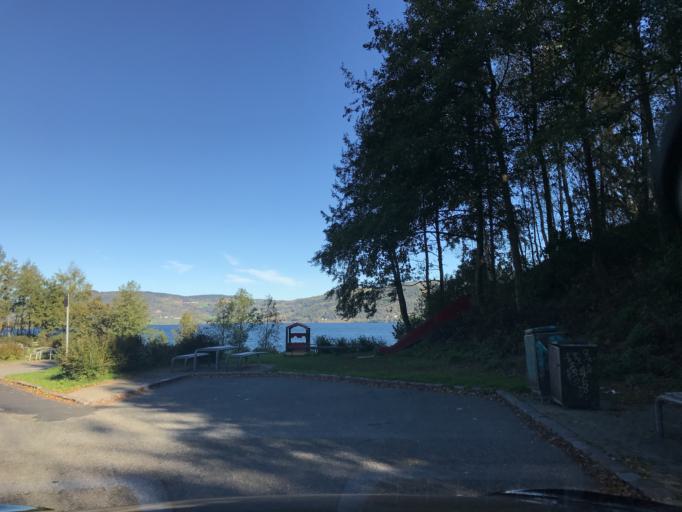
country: NO
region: Hedmark
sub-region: Ringsaker
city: Moelv
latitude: 60.9334
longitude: 10.6533
